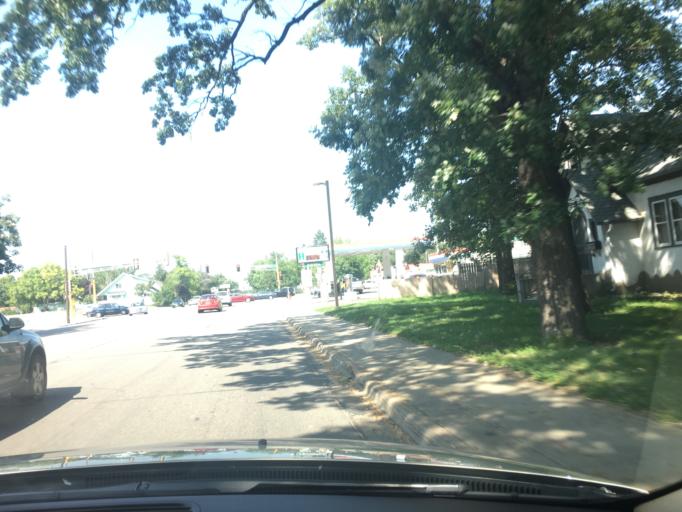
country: US
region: Minnesota
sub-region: Stearns County
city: Saint Cloud
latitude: 45.5486
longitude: -94.1601
